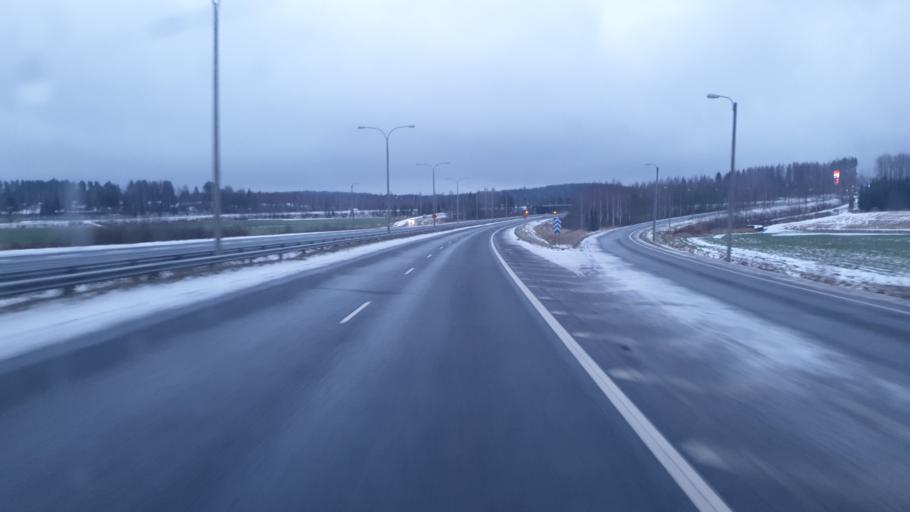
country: FI
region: Northern Savo
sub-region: Kuopio
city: Siilinjaervi
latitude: 62.9930
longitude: 27.7010
